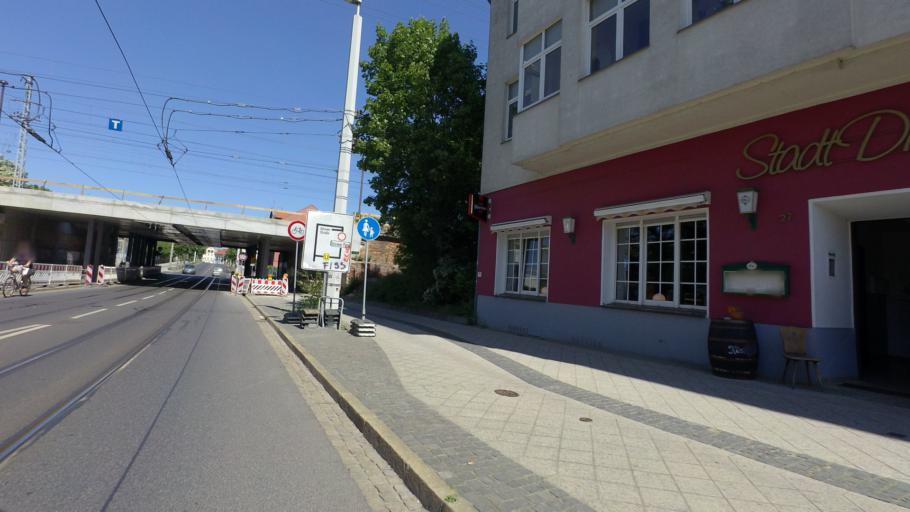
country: DE
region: Brandenburg
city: Cottbus
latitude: 51.7508
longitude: 14.3331
